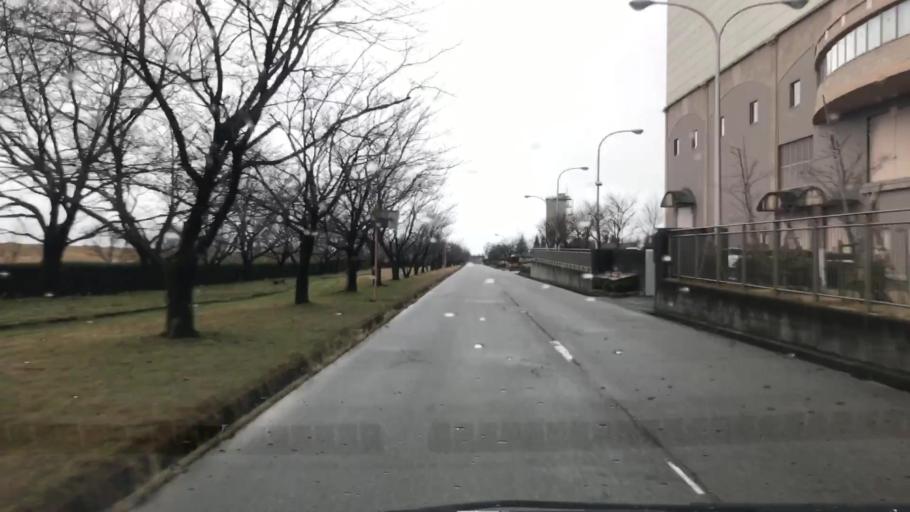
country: JP
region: Toyama
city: Kamiichi
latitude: 36.6209
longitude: 137.3044
